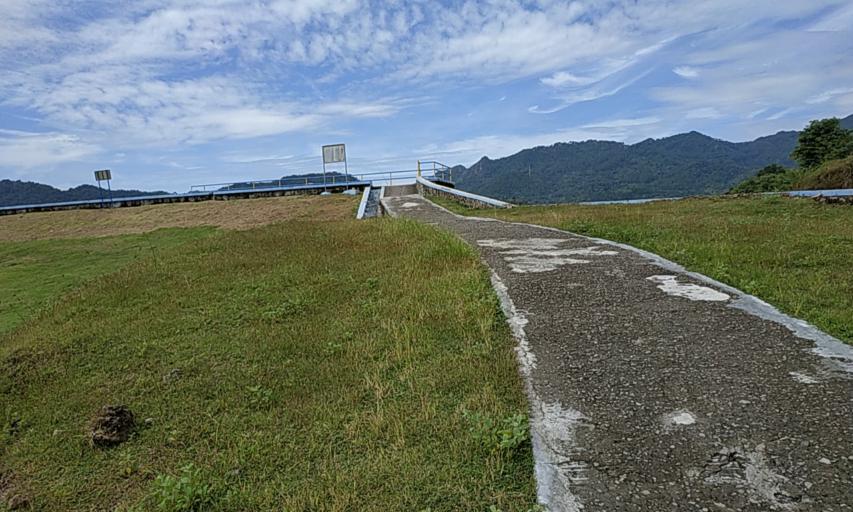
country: ID
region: Central Java
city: Selogiri
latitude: -7.8004
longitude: 110.8984
